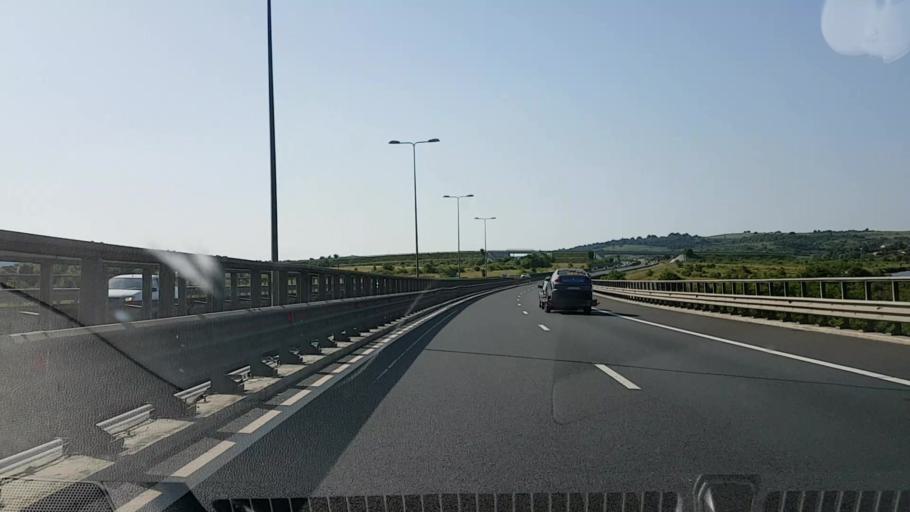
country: RO
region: Sibiu
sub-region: Comuna Orlat
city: Orlat
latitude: 45.7812
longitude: 23.9524
